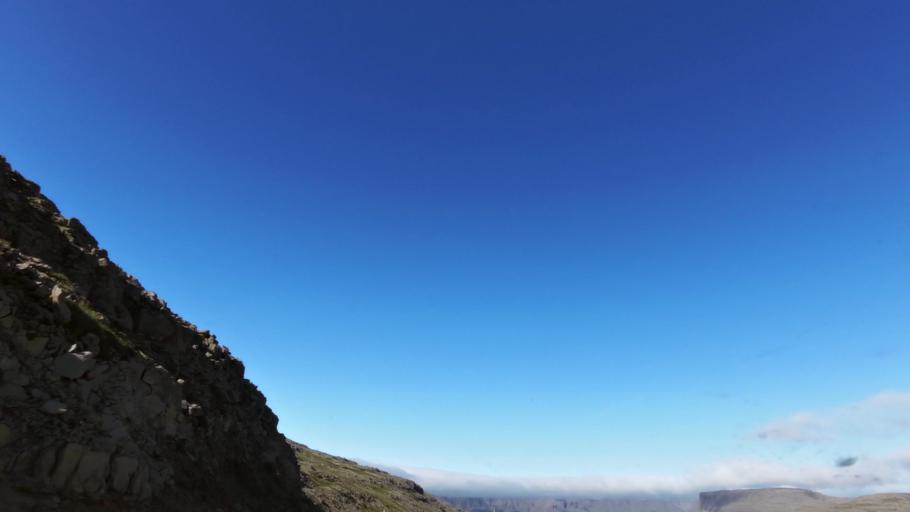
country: IS
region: West
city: Olafsvik
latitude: 65.5550
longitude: -24.1971
